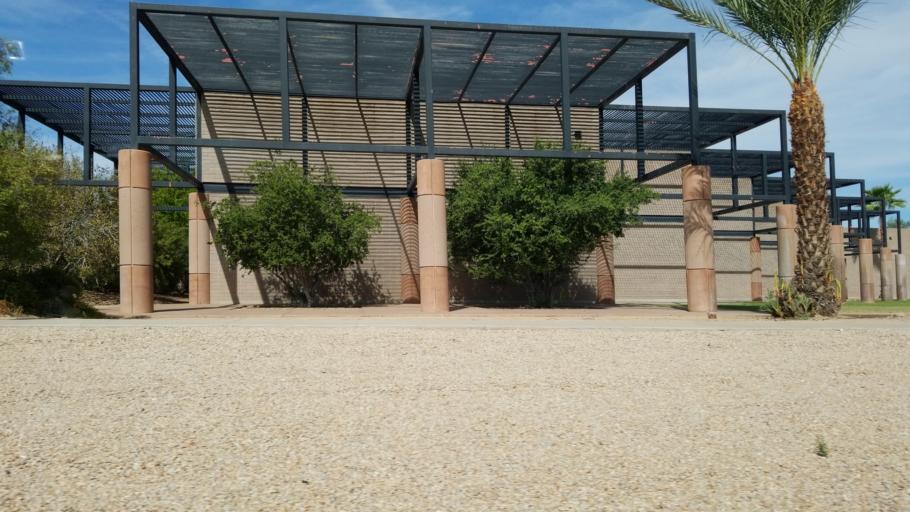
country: US
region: Arizona
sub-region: Maricopa County
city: Glendale
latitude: 33.5772
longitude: -112.1863
